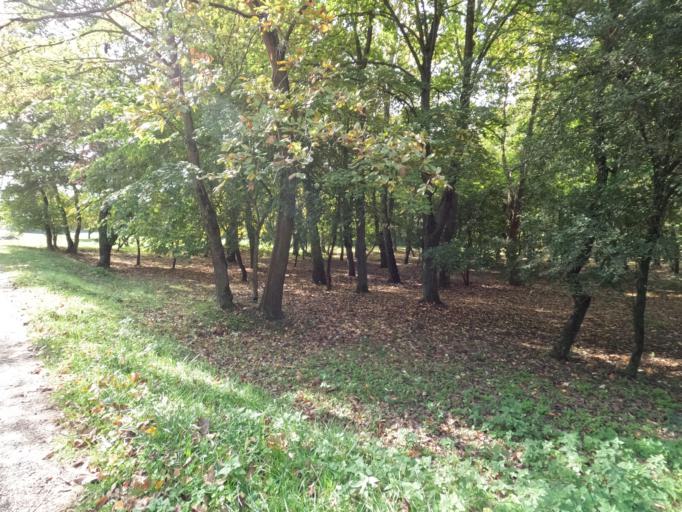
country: HU
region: Tolna
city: Szentgalpuszta
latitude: 46.3551
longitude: 18.6183
